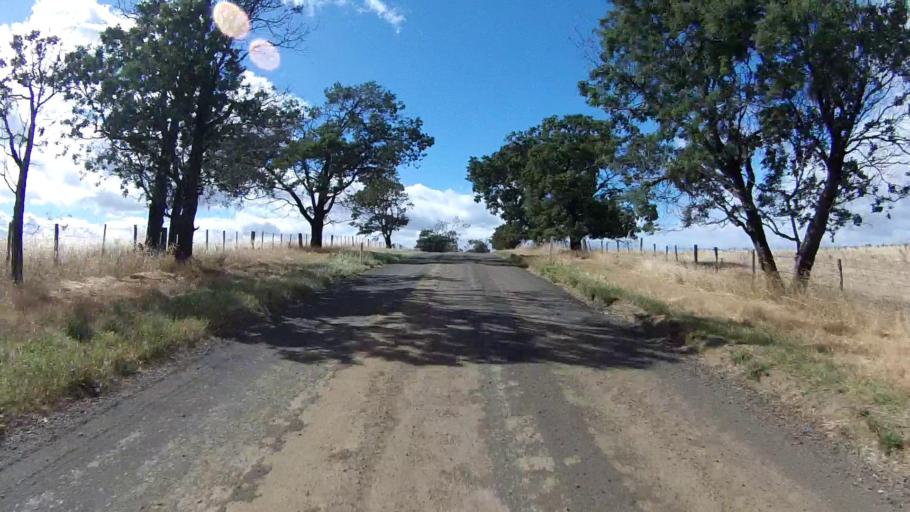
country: AU
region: Tasmania
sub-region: Northern Midlands
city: Evandale
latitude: -41.7239
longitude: 147.4352
